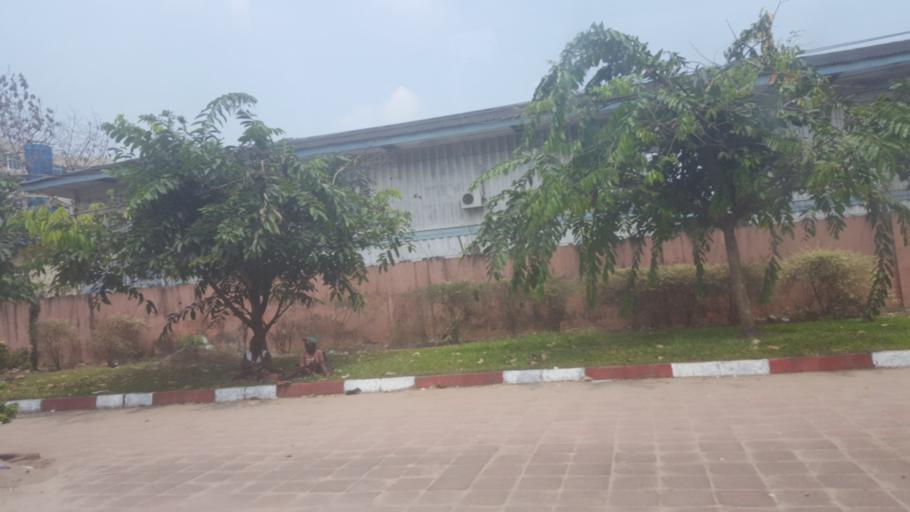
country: CD
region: Kinshasa
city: Kinshasa
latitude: -4.3065
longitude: 15.2987
